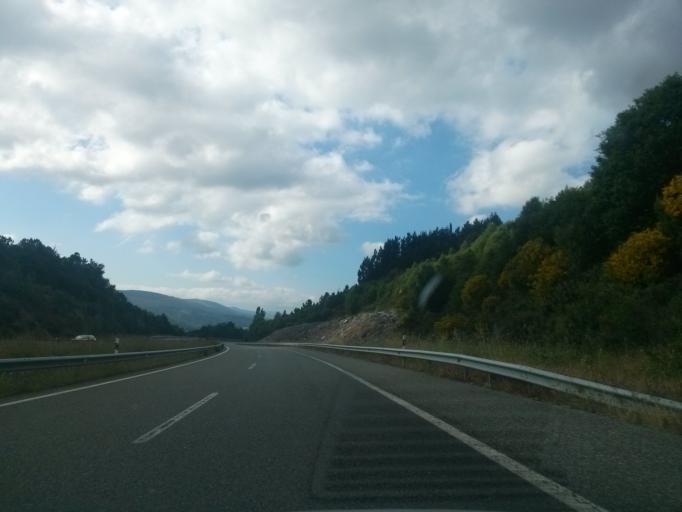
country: ES
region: Galicia
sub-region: Provincia de Lugo
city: Becerrea
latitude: 42.8937
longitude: -7.1844
